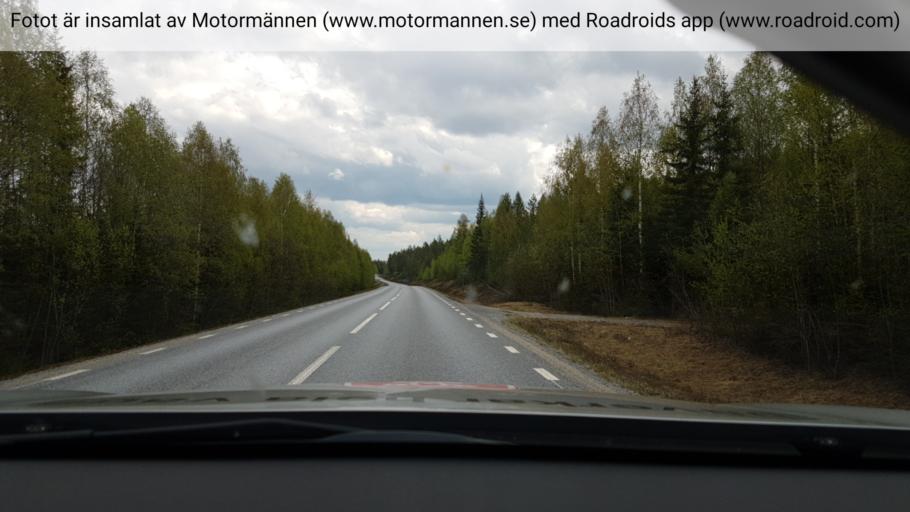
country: SE
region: Vaesterbotten
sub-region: Lycksele Kommun
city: Lycksele
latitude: 64.0346
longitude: 18.6165
